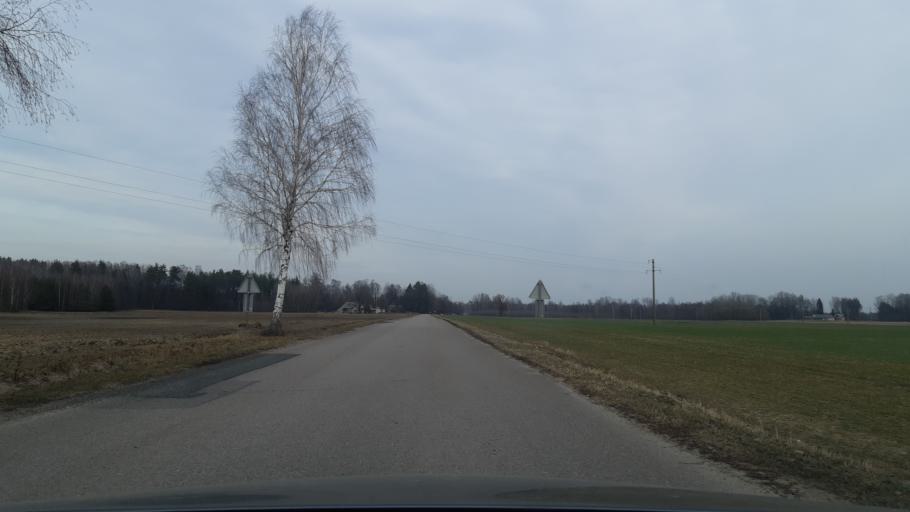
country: LT
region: Marijampoles apskritis
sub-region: Marijampole Municipality
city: Marijampole
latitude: 54.7283
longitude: 23.3369
